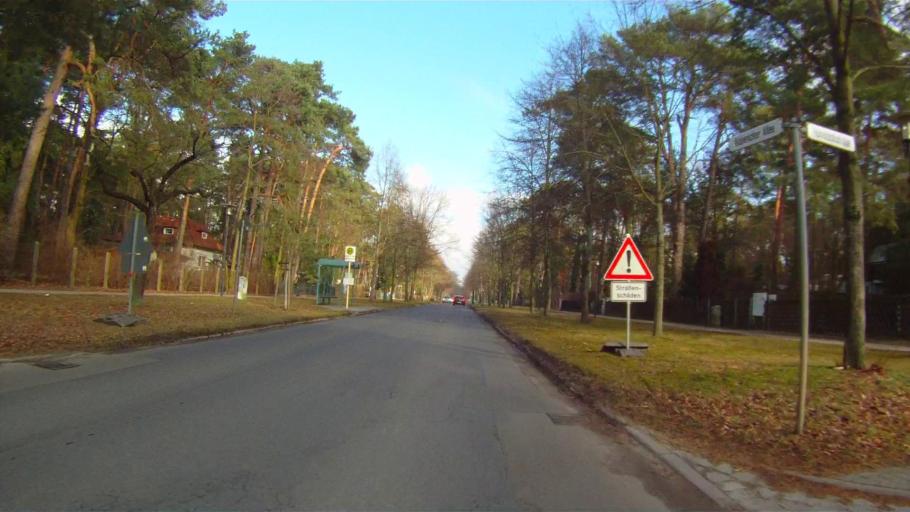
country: DE
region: Berlin
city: Friedrichshagen
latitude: 52.4803
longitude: 13.6235
